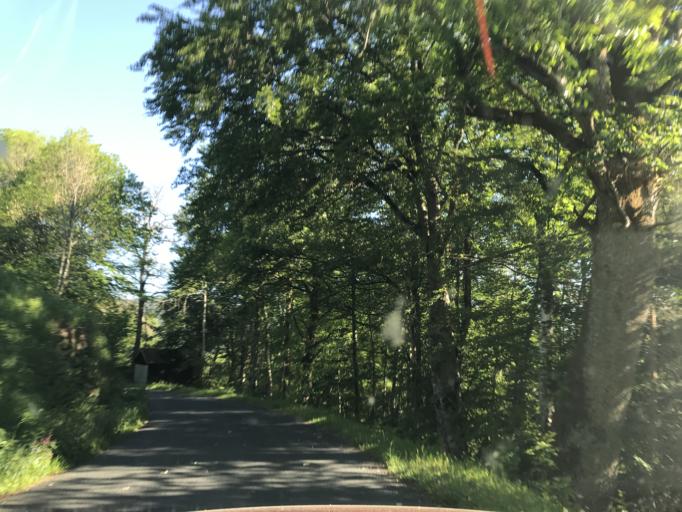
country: FR
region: Auvergne
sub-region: Departement du Puy-de-Dome
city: Job
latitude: 45.6977
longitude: 3.6897
